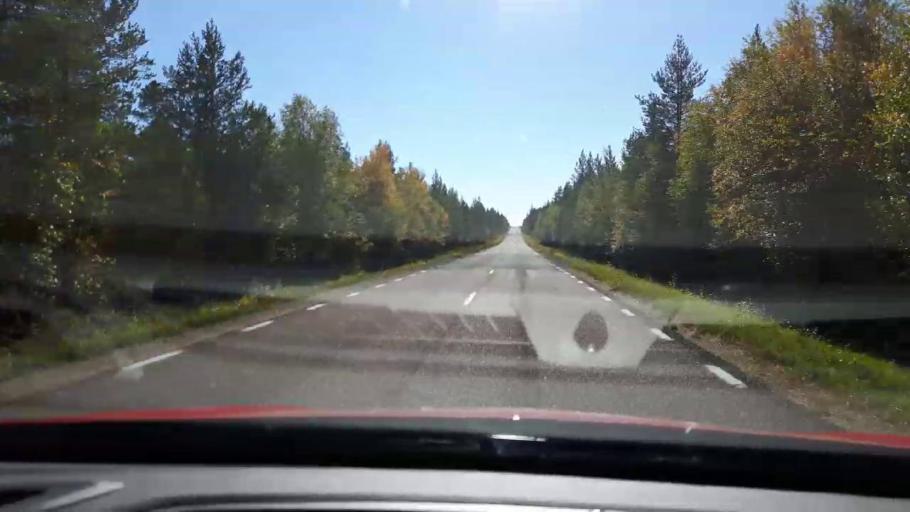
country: SE
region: Jaemtland
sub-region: Harjedalens Kommun
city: Sveg
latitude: 61.7372
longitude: 14.1631
